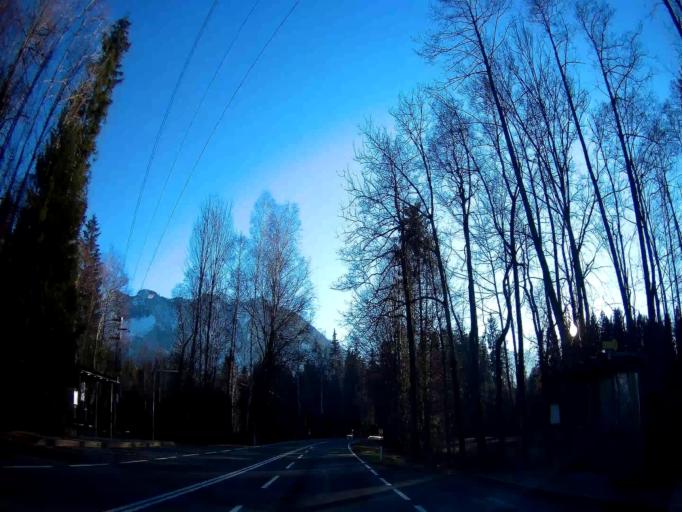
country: DE
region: Bavaria
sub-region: Upper Bavaria
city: Piding
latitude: 47.7518
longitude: 12.9440
